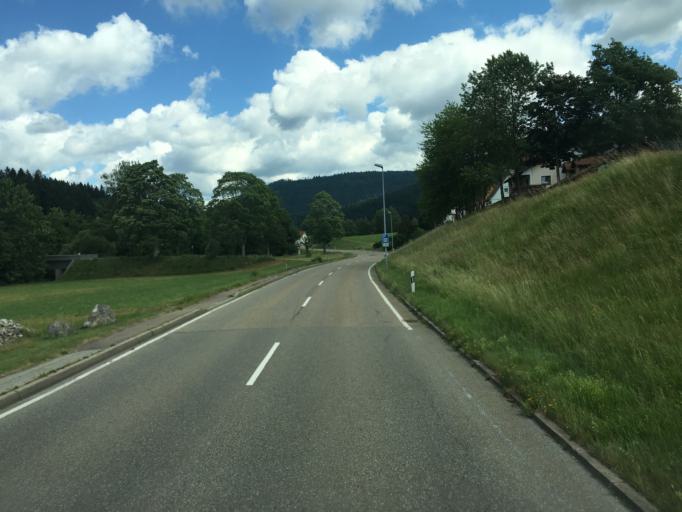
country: DE
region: Baden-Wuerttemberg
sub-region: Karlsruhe Region
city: Baiersbronn
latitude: 48.5640
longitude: 8.3952
